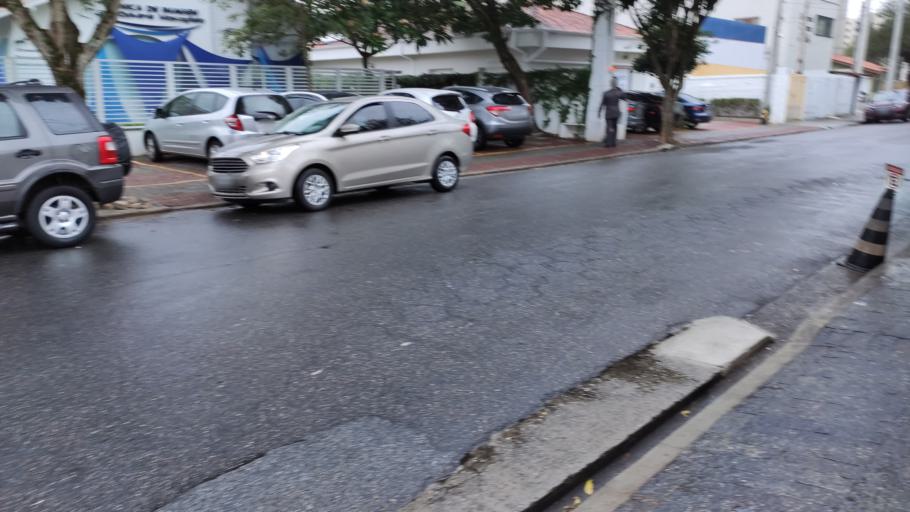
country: BR
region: Sao Paulo
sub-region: Sao Jose Dos Campos
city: Sao Jose dos Campos
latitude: -23.2062
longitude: -45.9023
